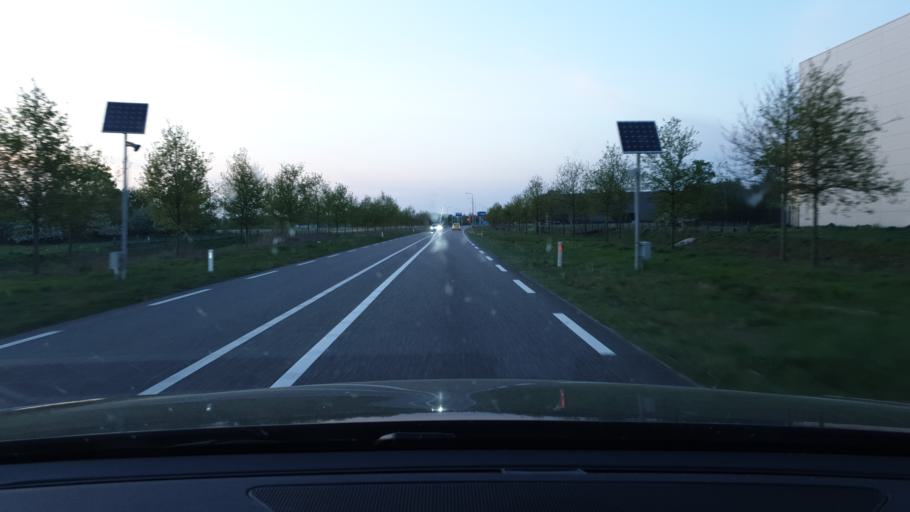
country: NL
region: North Brabant
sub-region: Gemeente Eersel
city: Eersel
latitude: 51.3591
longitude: 5.2714
